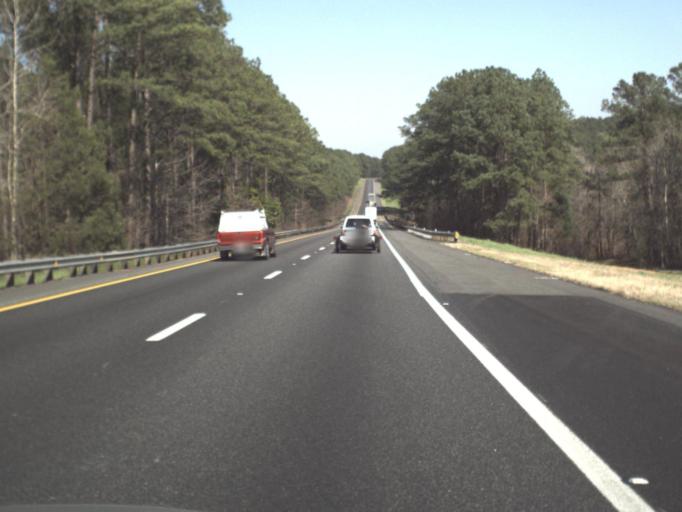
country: US
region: Florida
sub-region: Gadsden County
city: Chattahoochee
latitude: 30.6292
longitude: -84.8846
